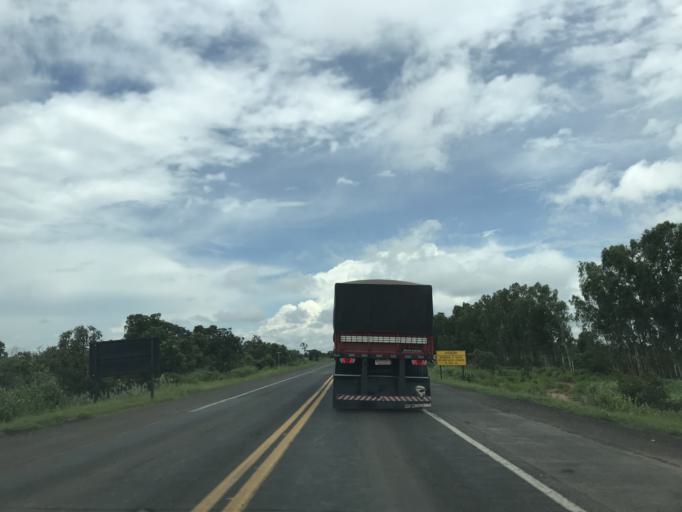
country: BR
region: Minas Gerais
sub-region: Frutal
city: Frutal
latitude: -19.7550
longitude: -48.9679
